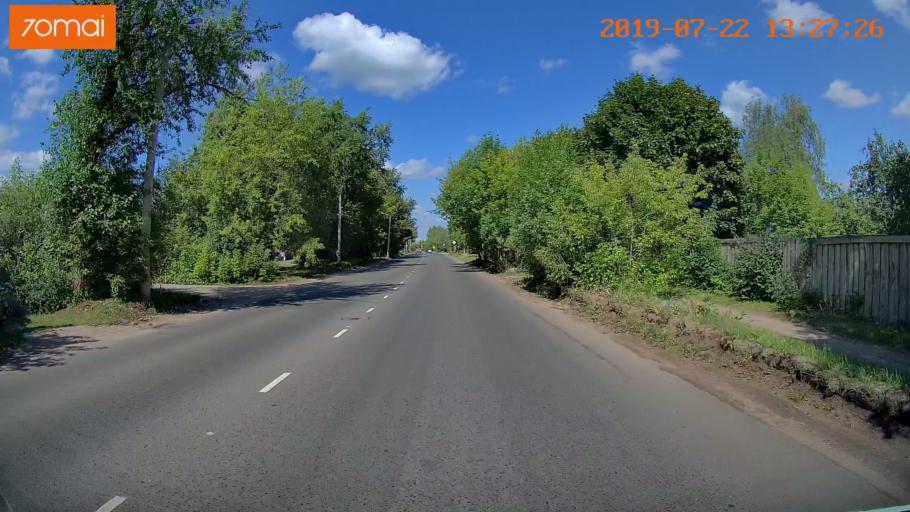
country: RU
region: Ivanovo
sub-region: Gorod Ivanovo
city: Ivanovo
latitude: 57.0348
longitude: 40.9501
